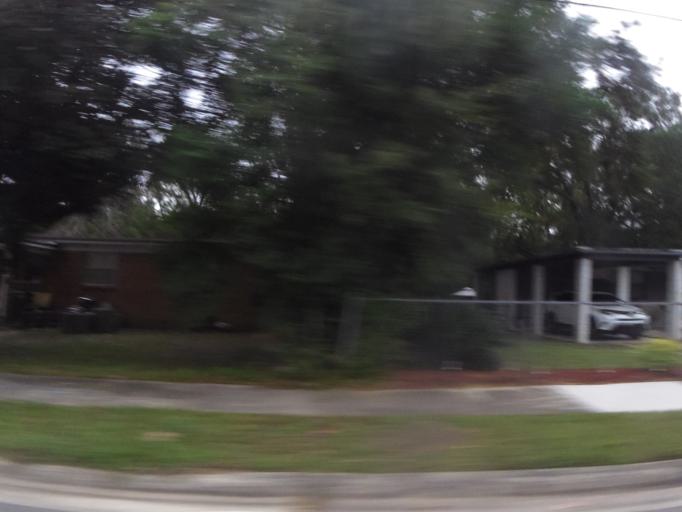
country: US
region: Florida
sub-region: Clay County
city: Bellair-Meadowbrook Terrace
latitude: 30.2651
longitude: -81.7474
